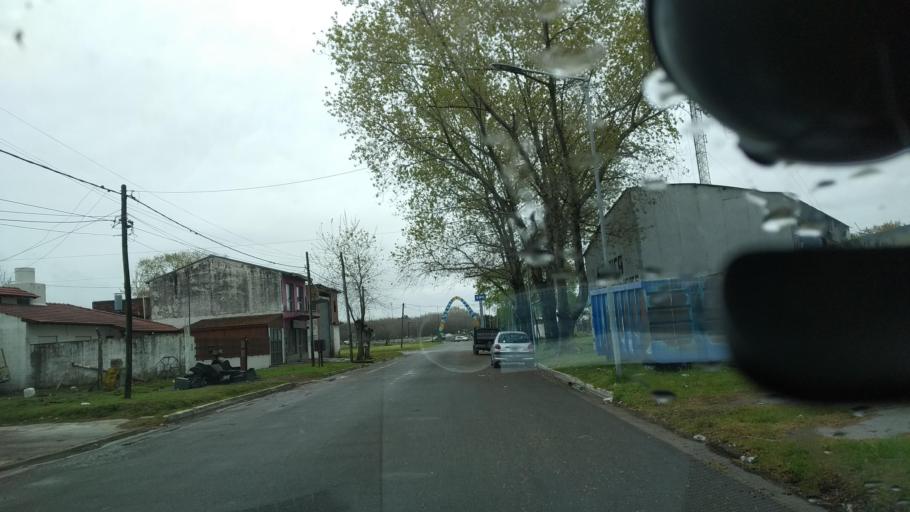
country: AR
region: Buenos Aires
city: Mar del Tuyu
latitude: -36.5349
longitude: -56.7136
